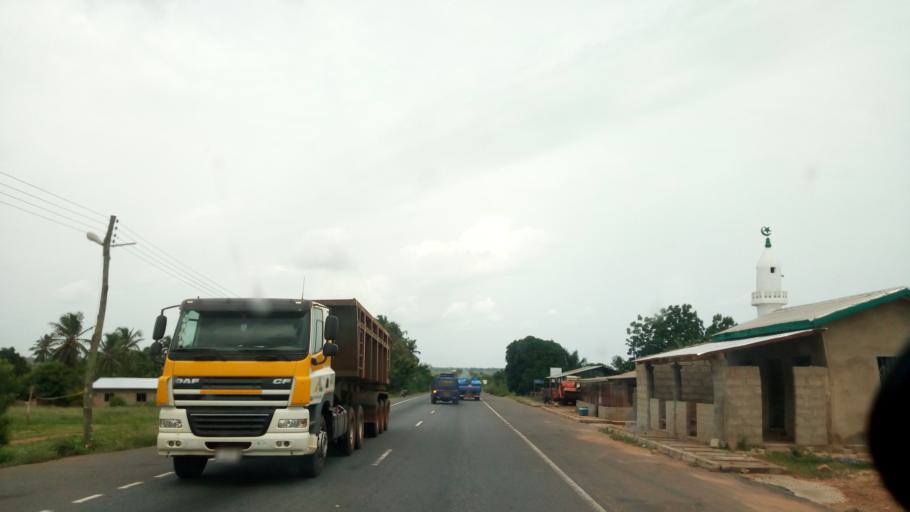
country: GH
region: Volta
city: Keta
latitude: 6.0641
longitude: 0.9193
